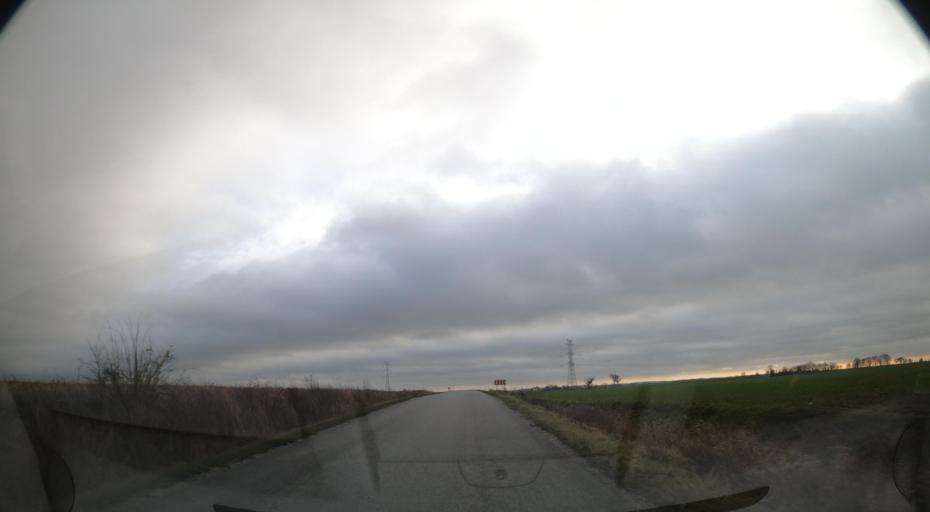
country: PL
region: Kujawsko-Pomorskie
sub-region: Powiat nakielski
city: Sadki
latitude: 53.1820
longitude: 17.4050
